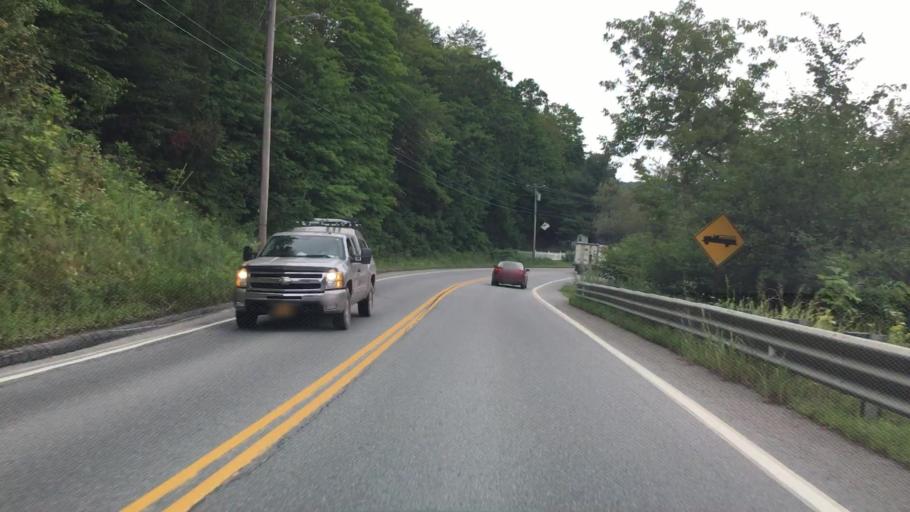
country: US
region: Maine
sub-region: Waldo County
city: Frankfort
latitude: 44.6060
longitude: -68.8726
